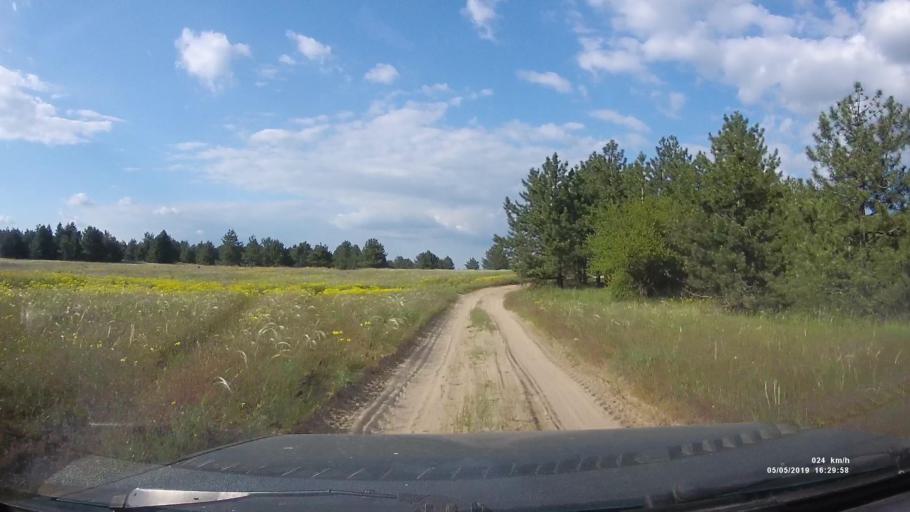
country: RU
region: Rostov
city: Ust'-Donetskiy
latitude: 47.7722
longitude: 41.0150
